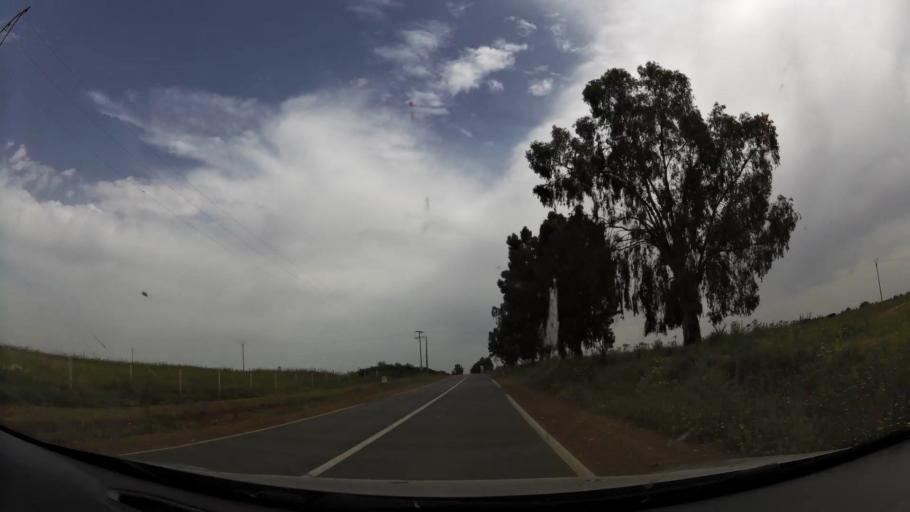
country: MA
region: Rabat-Sale-Zemmour-Zaer
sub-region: Khemisset
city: Tiflet
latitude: 33.8067
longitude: -6.2726
